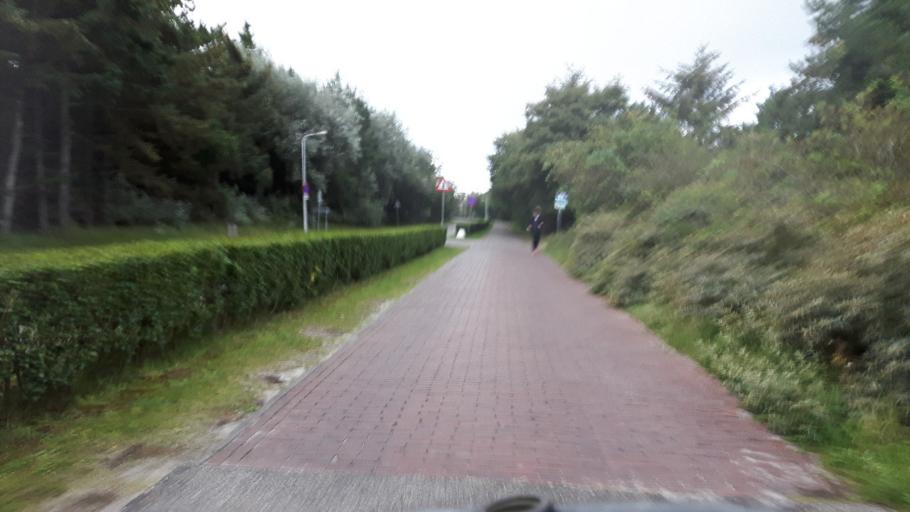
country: NL
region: Friesland
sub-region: Gemeente Ameland
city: Nes
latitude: 53.4557
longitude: 5.7775
